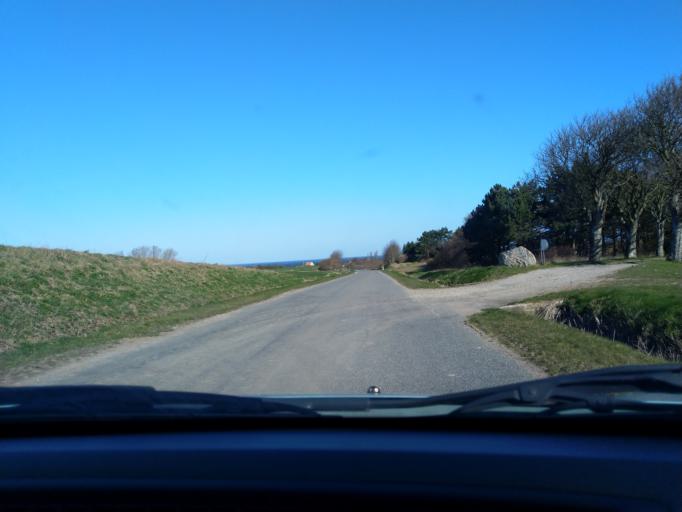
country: DK
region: Zealand
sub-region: Kalundborg Kommune
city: Kalundborg
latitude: 55.7432
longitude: 10.9529
